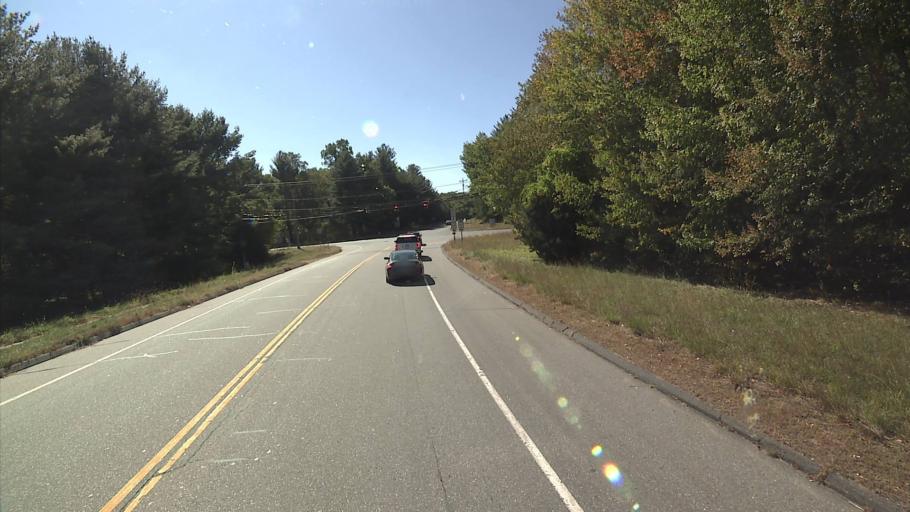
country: US
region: Connecticut
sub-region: Hartford County
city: Manchester
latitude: 41.7129
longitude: -72.5266
